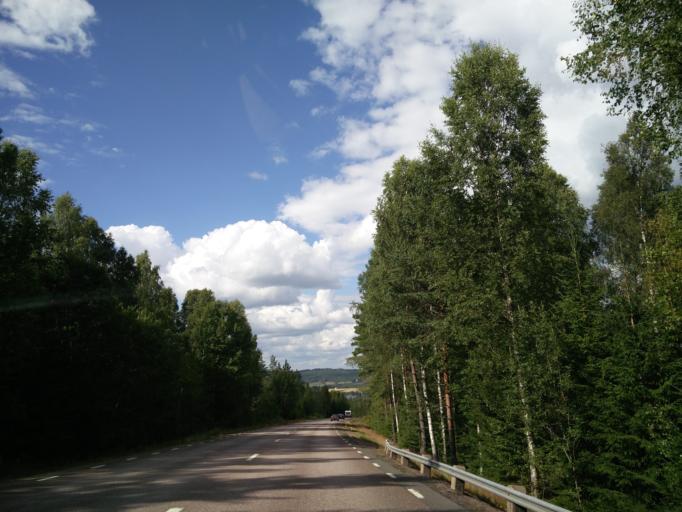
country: SE
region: Vaermland
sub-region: Sunne Kommun
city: Sunne
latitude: 59.7030
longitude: 13.1062
